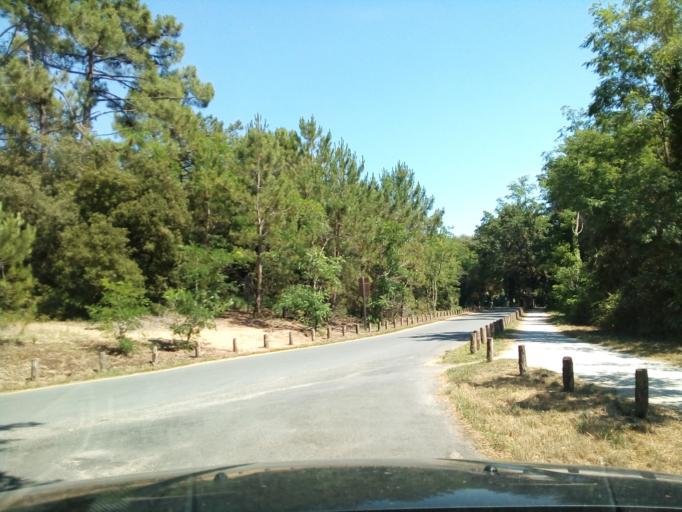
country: FR
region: Poitou-Charentes
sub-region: Departement de la Charente-Maritime
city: Boyard-Ville
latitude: 45.9821
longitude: -1.2950
